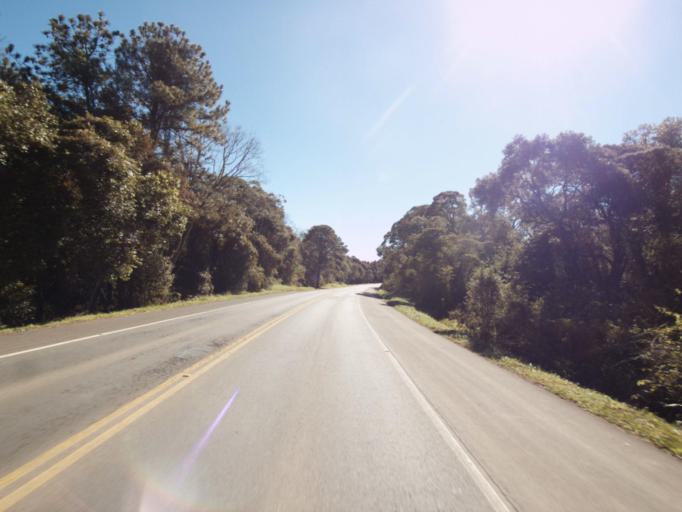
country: BR
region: Santa Catarina
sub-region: Joacaba
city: Joacaba
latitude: -27.1215
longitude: -51.6323
